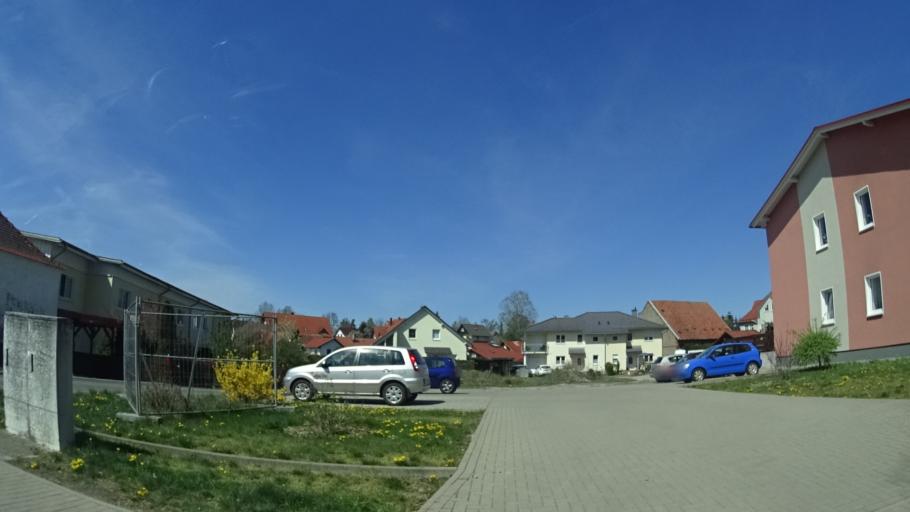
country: DE
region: Thuringia
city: Hildburghausen
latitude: 50.4264
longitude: 10.7378
